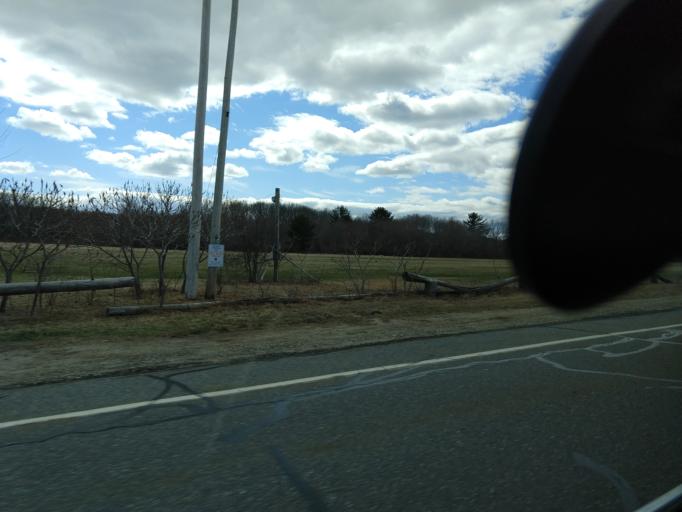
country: US
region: Massachusetts
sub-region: Essex County
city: Newburyport
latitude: 42.7967
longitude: -70.8428
